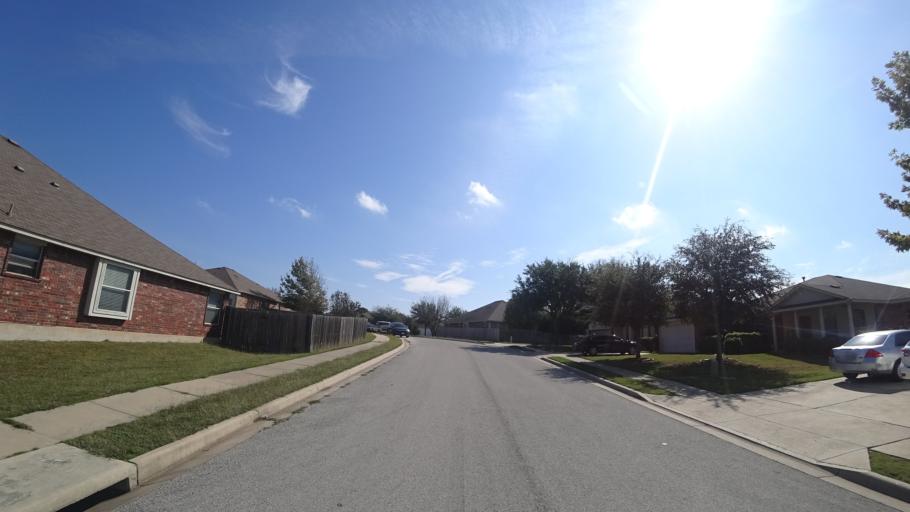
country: US
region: Texas
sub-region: Travis County
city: Pflugerville
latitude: 30.4198
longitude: -97.6360
